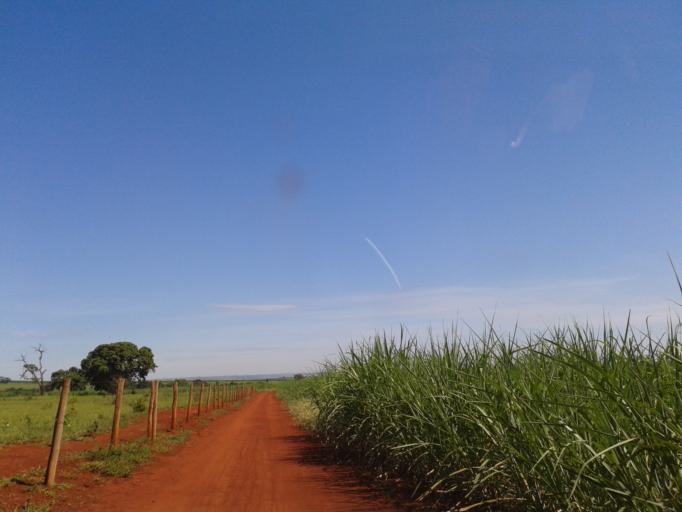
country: BR
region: Minas Gerais
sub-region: Centralina
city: Centralina
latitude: -18.6315
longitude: -49.2521
